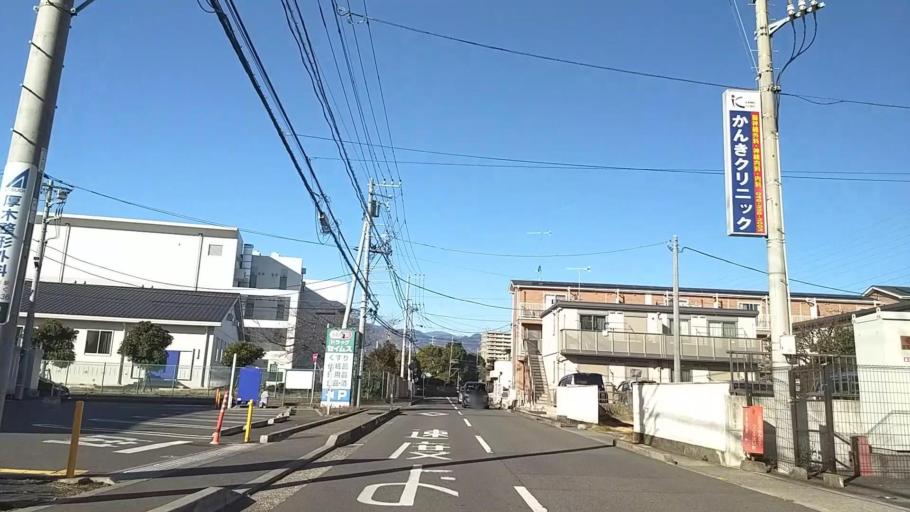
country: JP
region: Kanagawa
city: Atsugi
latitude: 35.4314
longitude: 139.3628
